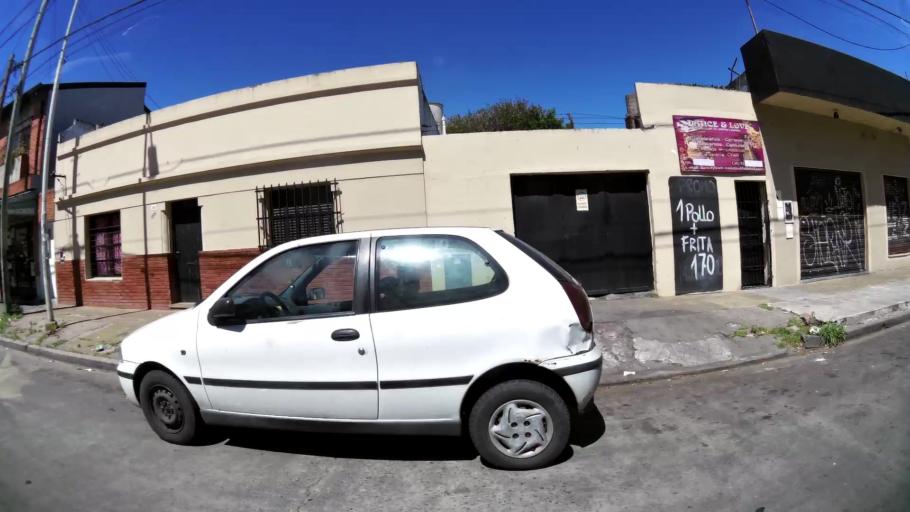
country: AR
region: Buenos Aires
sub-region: Partido de General San Martin
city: General San Martin
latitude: -34.5295
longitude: -58.5547
